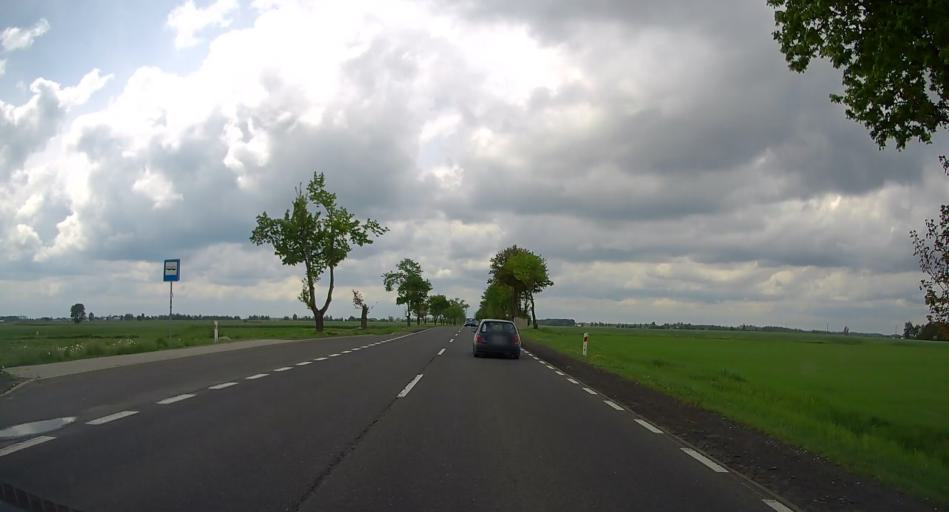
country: PL
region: Masovian Voivodeship
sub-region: Powiat plonski
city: Czerwinsk Nad Wisla
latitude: 52.4241
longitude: 20.4300
